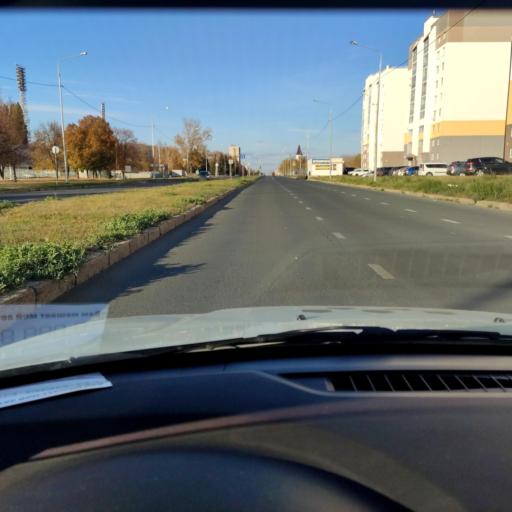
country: RU
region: Samara
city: Tol'yatti
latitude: 53.5006
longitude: 49.2693
